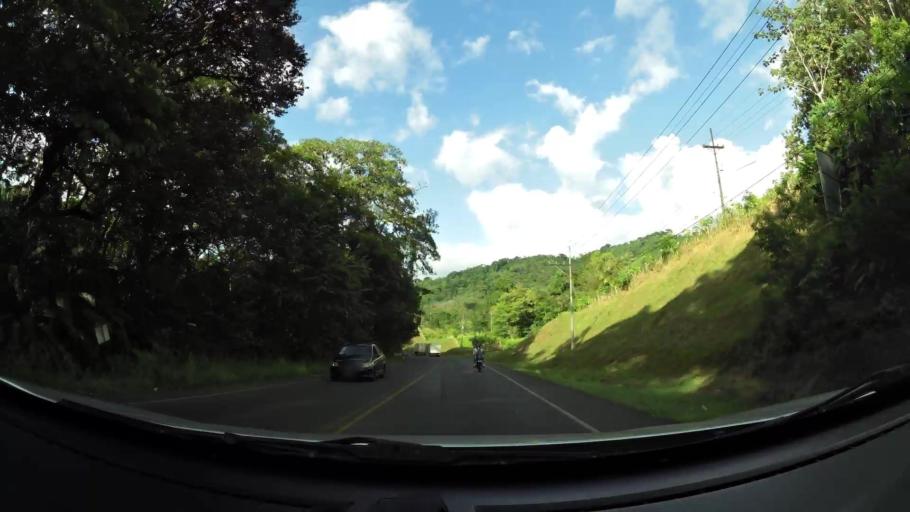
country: CR
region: Puntarenas
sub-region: Canton de Garabito
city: Jaco
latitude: 9.7259
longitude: -84.6265
